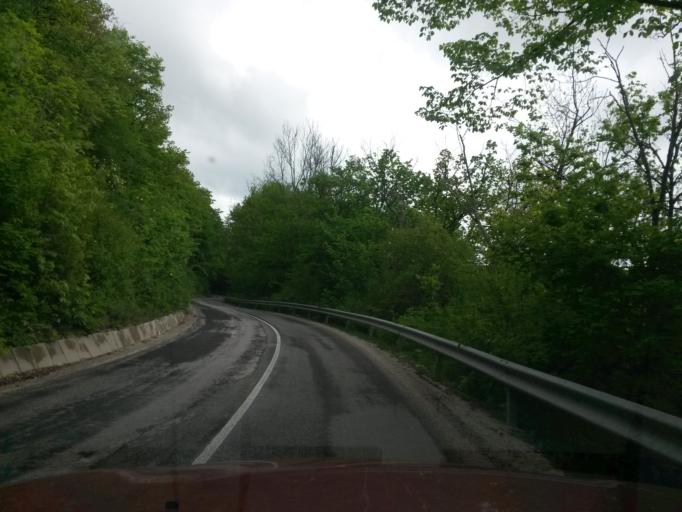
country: SK
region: Kosicky
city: Roznava
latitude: 48.5681
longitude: 20.4712
